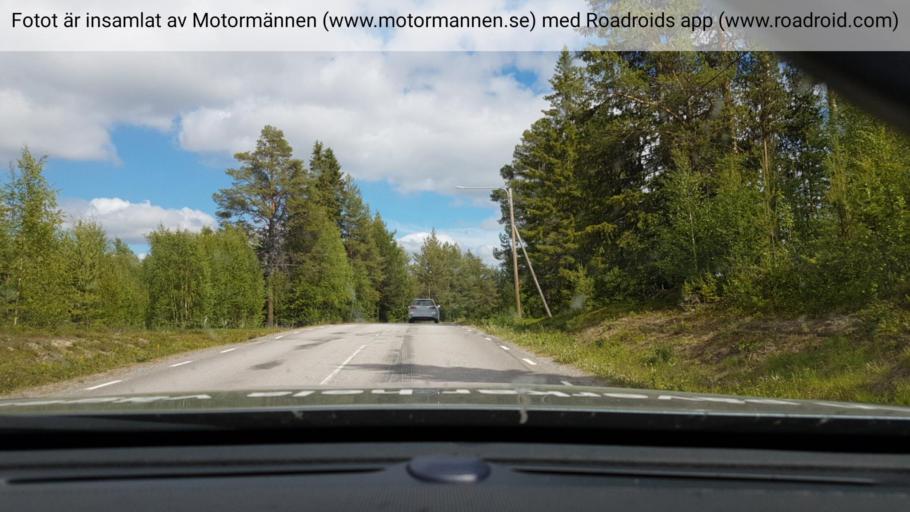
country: SE
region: Vaesterbotten
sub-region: Sorsele Kommun
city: Sorsele
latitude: 65.6005
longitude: 17.4897
